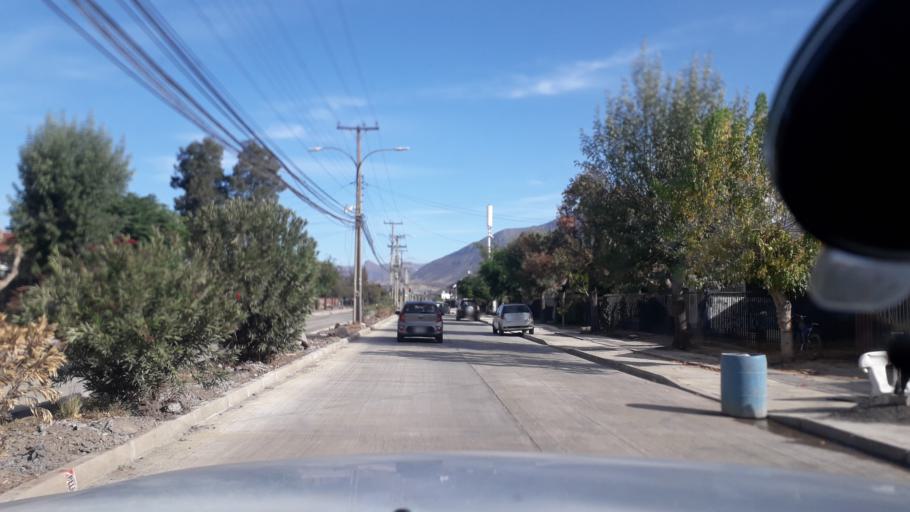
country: CL
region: Valparaiso
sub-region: Provincia de San Felipe
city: San Felipe
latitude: -32.7508
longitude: -70.7112
